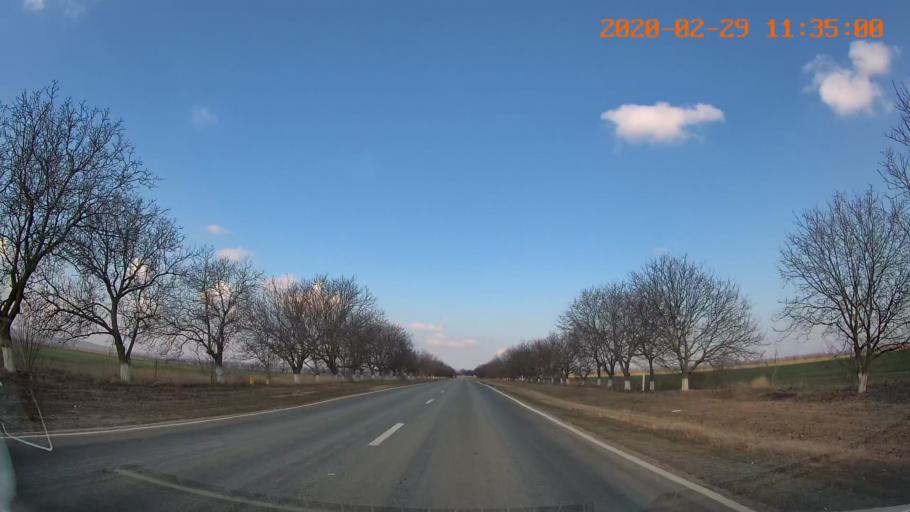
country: MD
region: Rezina
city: Saharna
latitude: 47.5737
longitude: 29.0678
